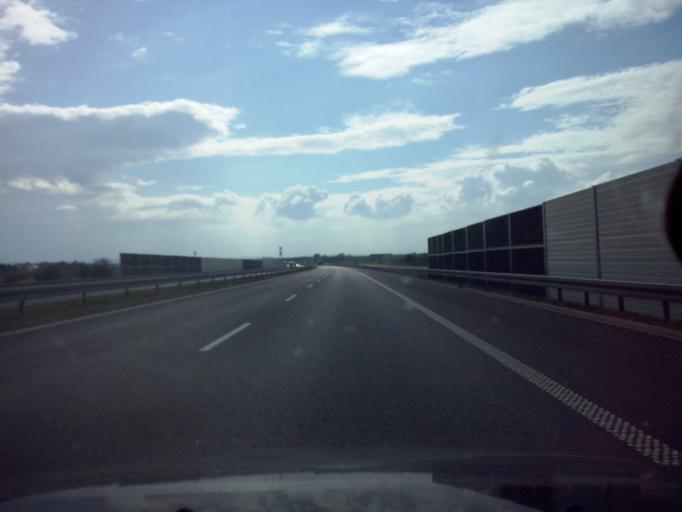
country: PL
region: Lesser Poland Voivodeship
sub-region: Powiat tarnowski
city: Wierzchoslawice
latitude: 50.0498
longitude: 20.9040
